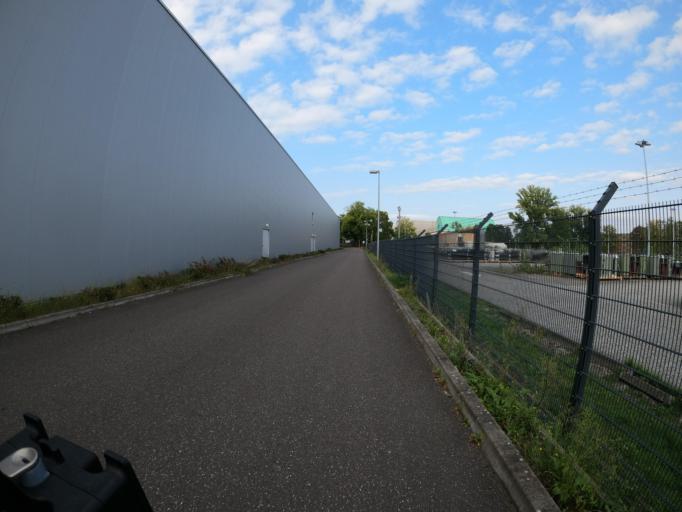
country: DE
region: Berlin
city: Siemensstadt
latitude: 52.5394
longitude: 13.2513
